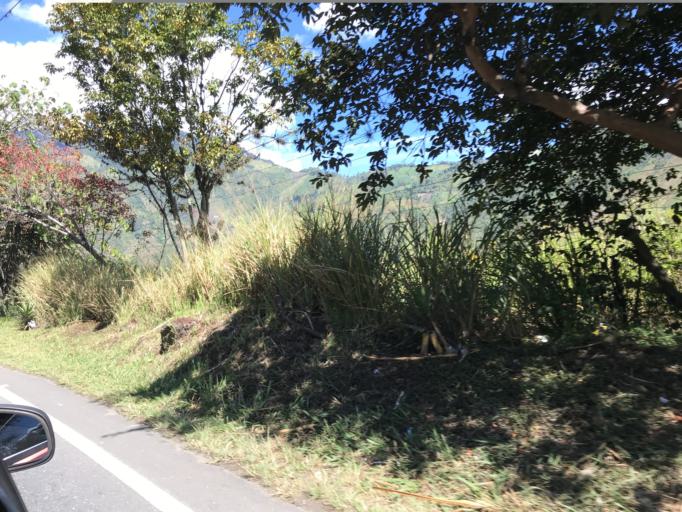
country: CO
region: Tolima
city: Cajamarca
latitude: 4.4410
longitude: -75.4045
